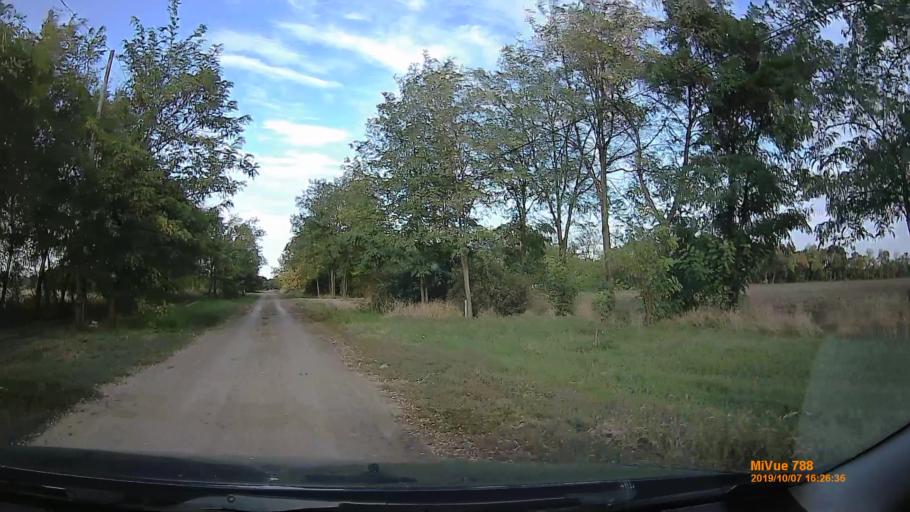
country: HU
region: Bekes
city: Szarvas
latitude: 46.8201
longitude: 20.6394
